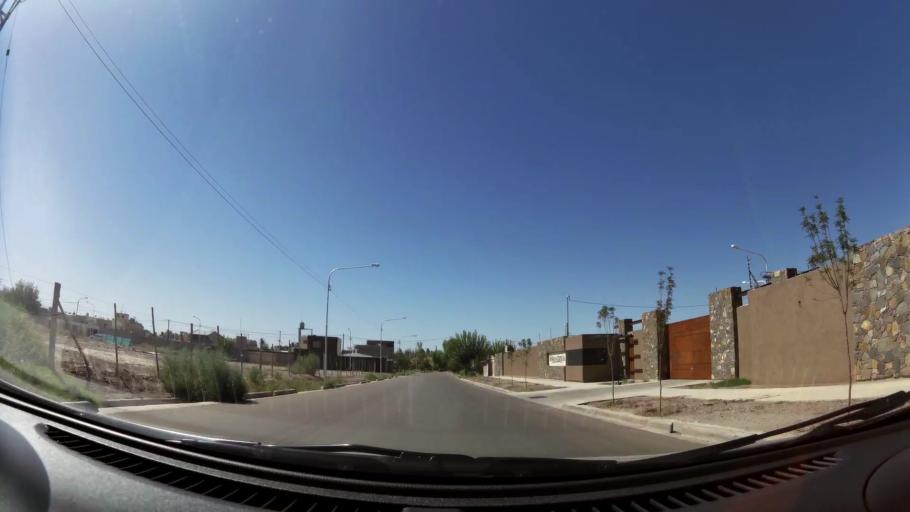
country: AR
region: Mendoza
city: Villa Nueva
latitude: -32.9018
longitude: -68.7769
